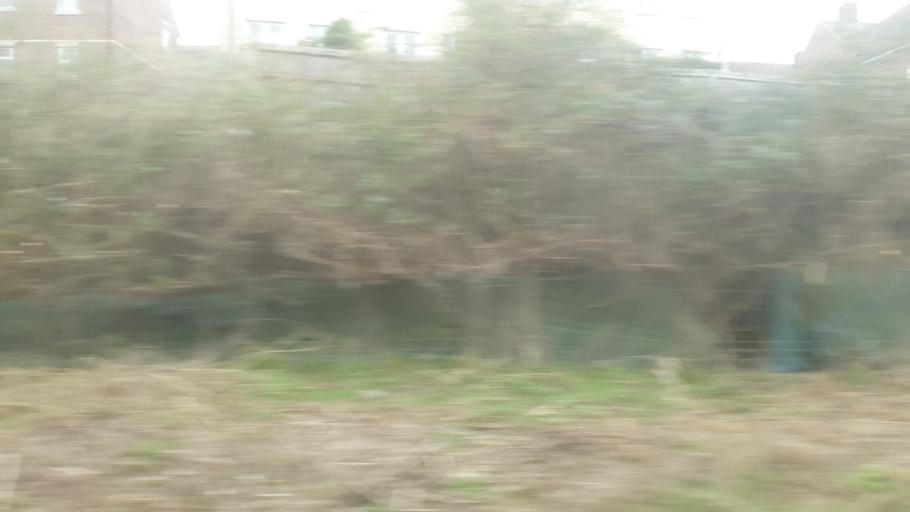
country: GB
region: England
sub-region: West Sussex
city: Pulborough
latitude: 50.9644
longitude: -0.5012
